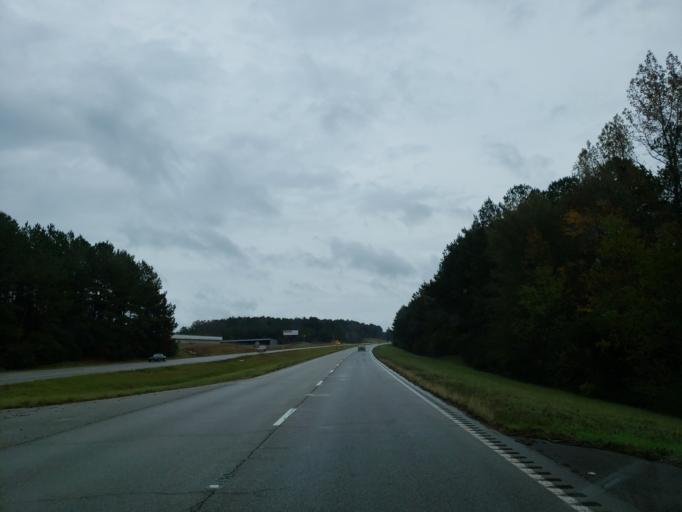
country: US
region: Mississippi
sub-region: Jones County
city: Laurel
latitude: 31.7054
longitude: -89.0722
